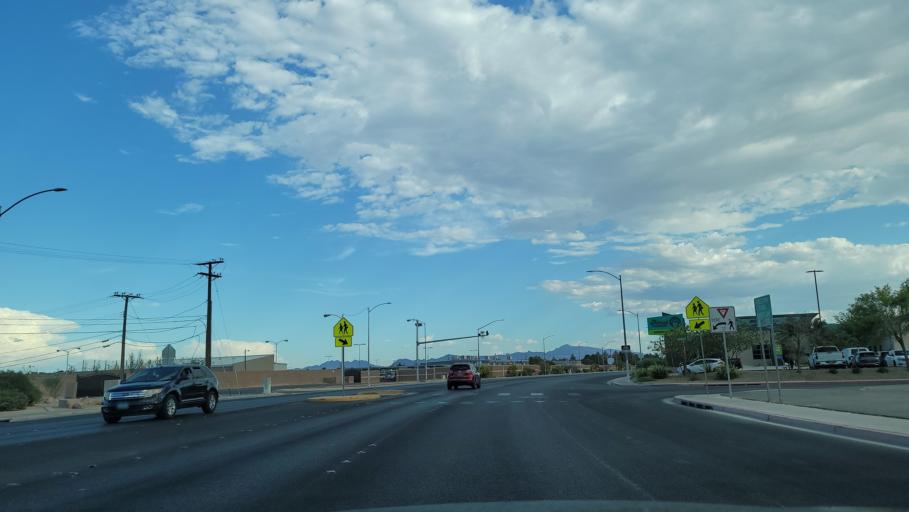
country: US
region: Nevada
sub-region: Clark County
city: North Las Vegas
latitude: 36.1779
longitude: -115.1062
